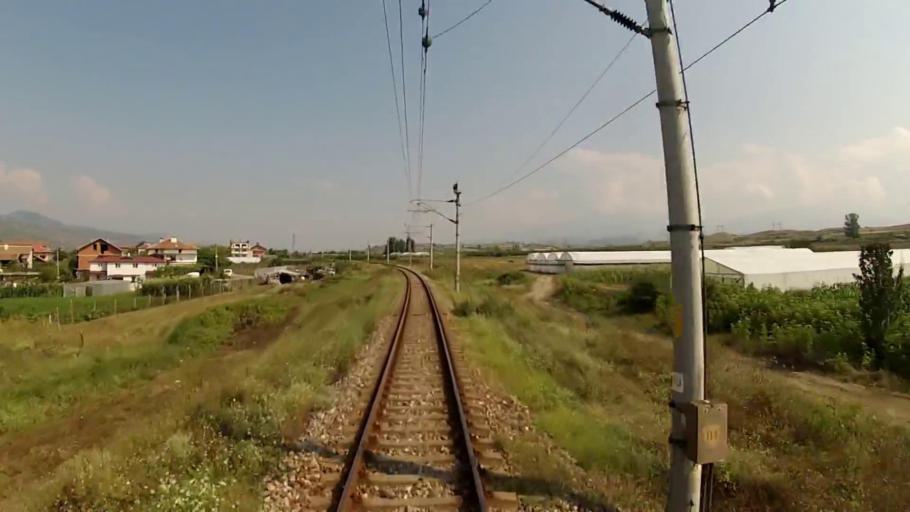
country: BG
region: Blagoevgrad
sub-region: Obshtina Sandanski
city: Sandanski
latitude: 41.5109
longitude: 23.2689
